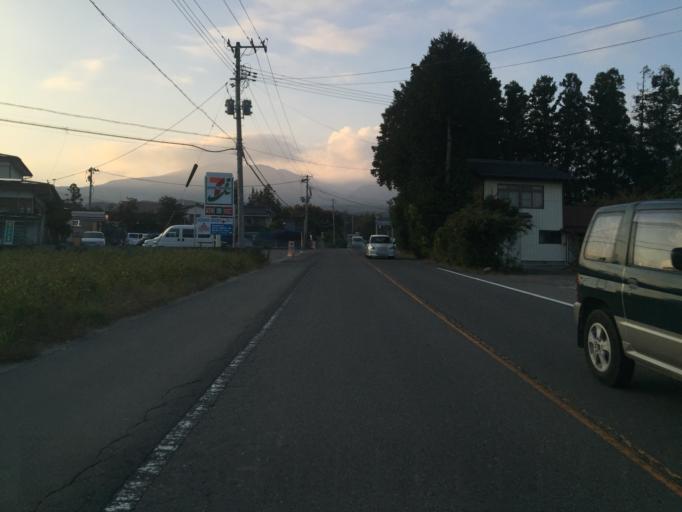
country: JP
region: Fukushima
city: Motomiya
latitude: 37.5562
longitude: 140.3559
